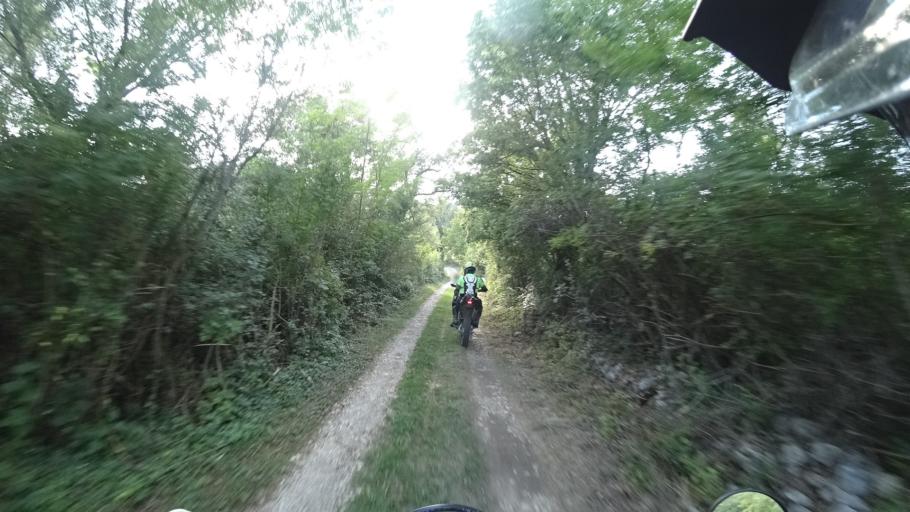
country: HR
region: Sibensko-Kniniska
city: Knin
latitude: 44.2034
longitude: 16.0715
